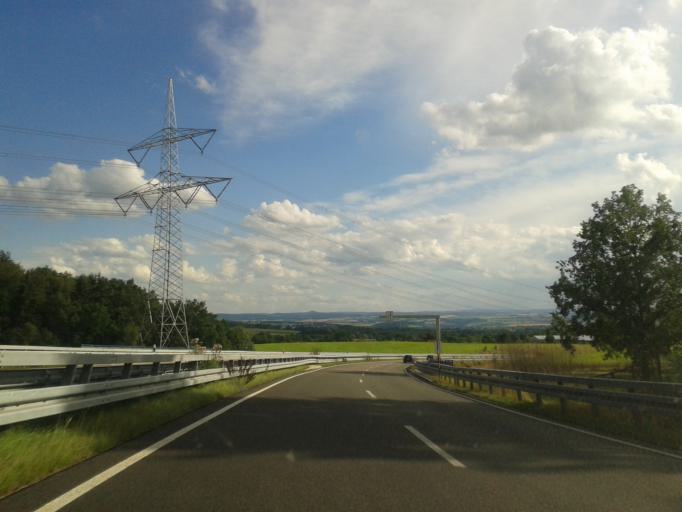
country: DE
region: Saxony
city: Durrrohrsdorf
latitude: 51.0064
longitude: 13.9594
